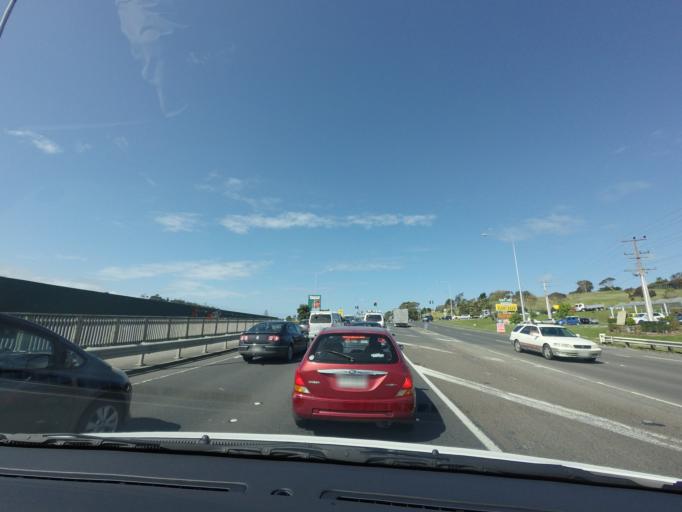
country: NZ
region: Auckland
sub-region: Auckland
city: Rothesay Bay
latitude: -36.6218
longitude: 174.6705
